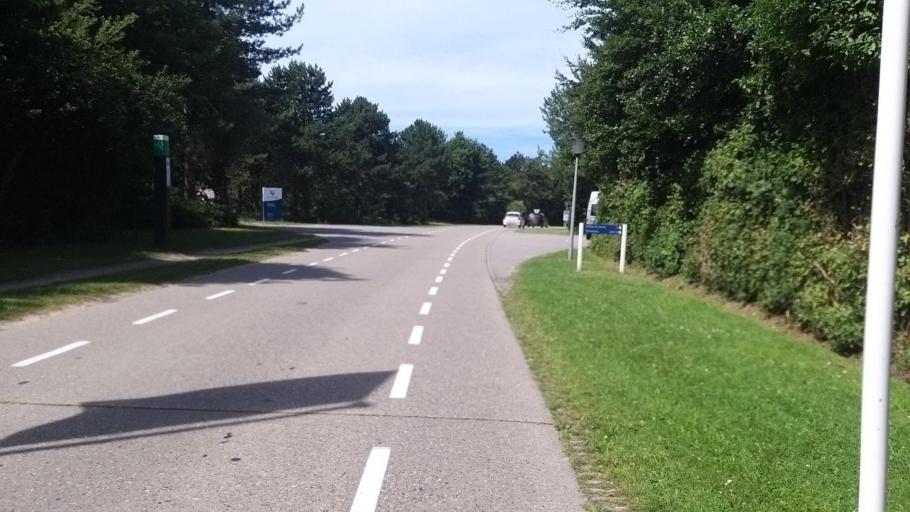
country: NL
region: North Holland
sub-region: Gemeente Texel
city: Den Burg
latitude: 53.1491
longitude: 4.8622
